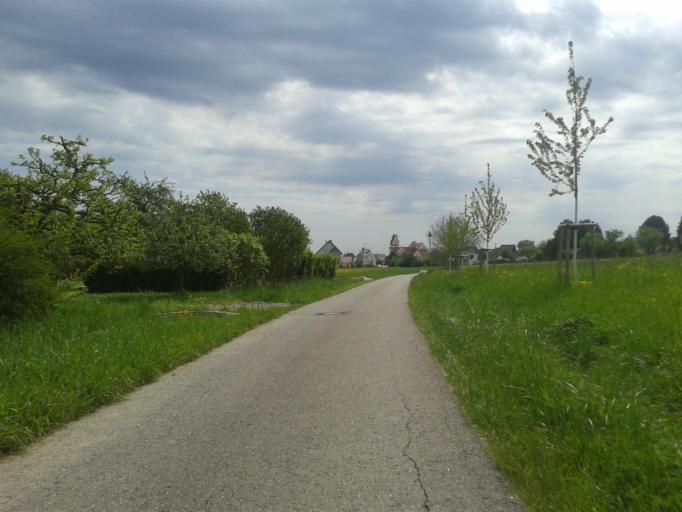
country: DE
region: Baden-Wuerttemberg
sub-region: Tuebingen Region
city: Erbach
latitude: 48.3544
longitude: 9.8889
